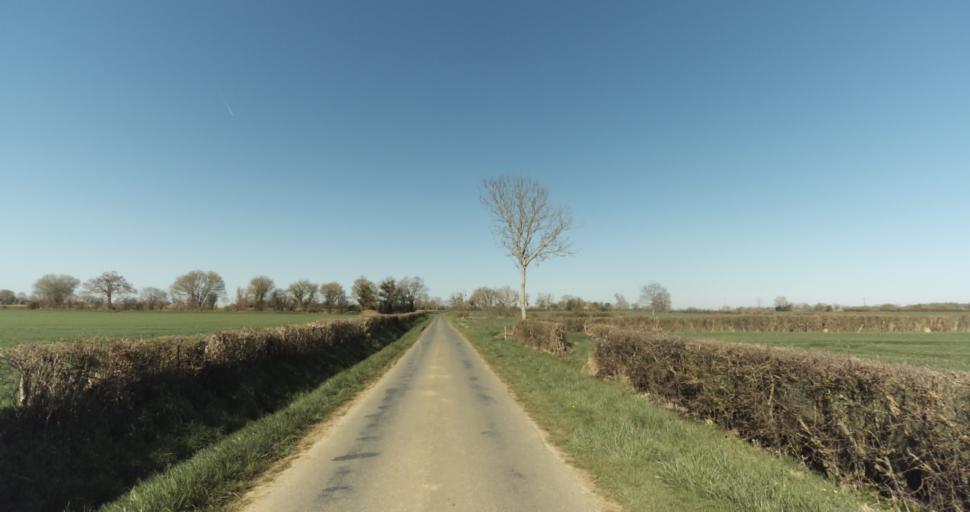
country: FR
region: Lower Normandy
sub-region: Departement du Calvados
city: Saint-Pierre-sur-Dives
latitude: 48.9672
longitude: 0.0147
